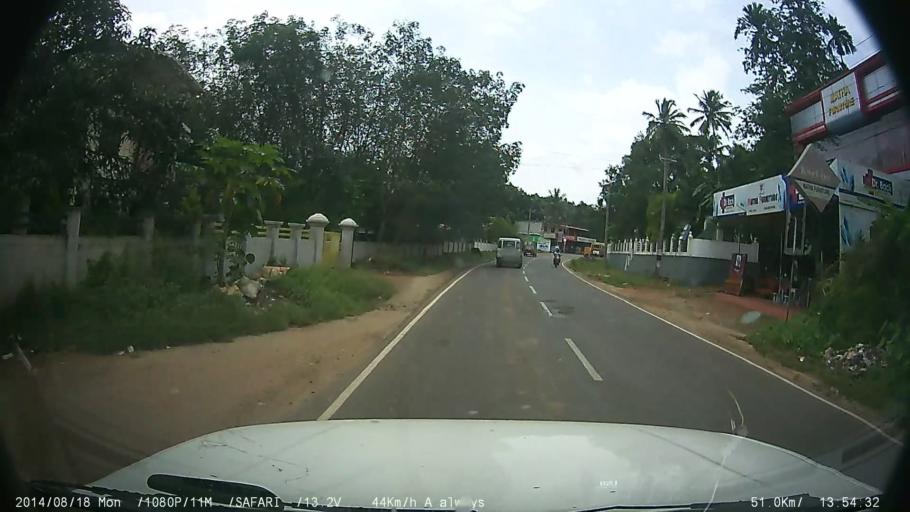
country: IN
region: Kerala
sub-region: Kottayam
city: Palackattumala
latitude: 9.7402
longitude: 76.5605
